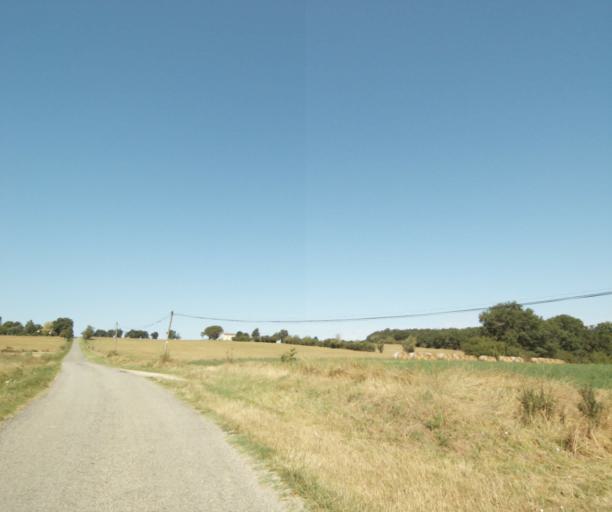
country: FR
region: Midi-Pyrenees
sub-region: Departement de l'Ariege
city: Lezat-sur-Leze
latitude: 43.2991
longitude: 1.3348
